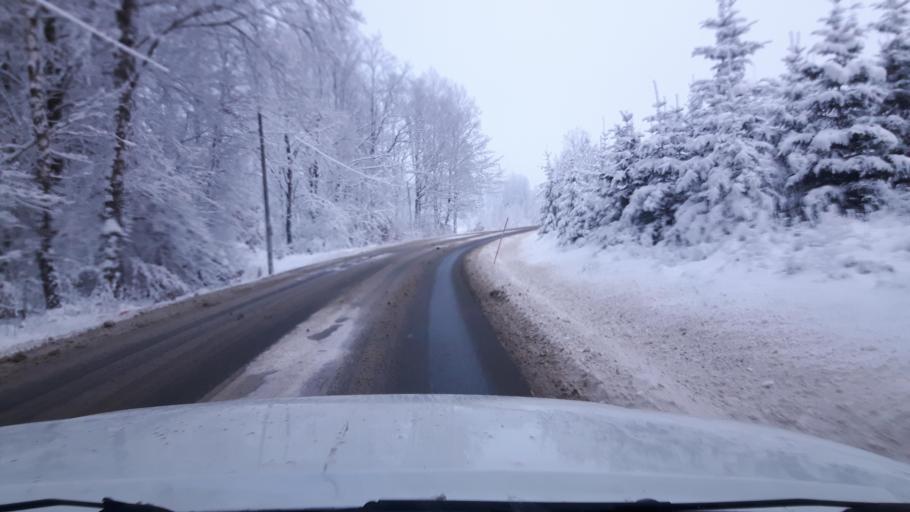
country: SE
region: Halland
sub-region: Kungsbacka Kommun
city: Fjaeras kyrkby
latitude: 57.4693
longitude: 12.2151
